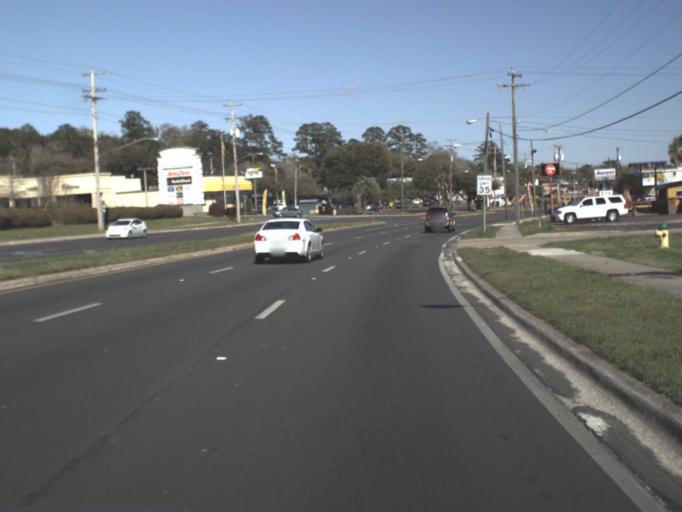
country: US
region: Florida
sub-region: Leon County
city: Tallahassee
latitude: 30.4487
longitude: -84.3166
